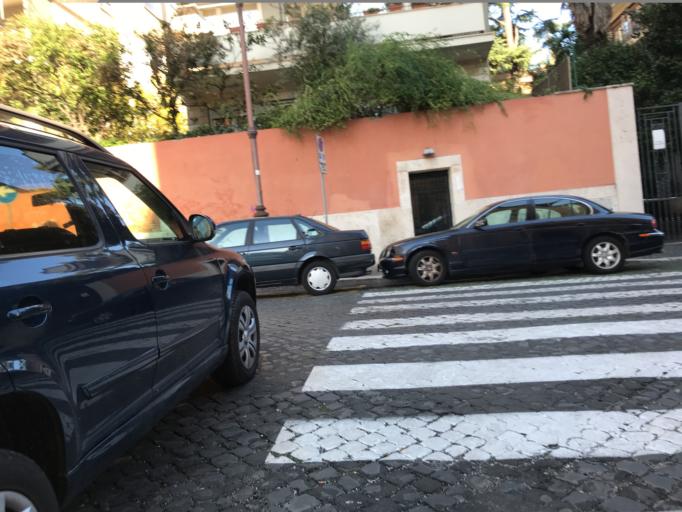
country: IT
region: Latium
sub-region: Citta metropolitana di Roma Capitale
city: Rome
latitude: 41.9135
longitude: 12.5011
